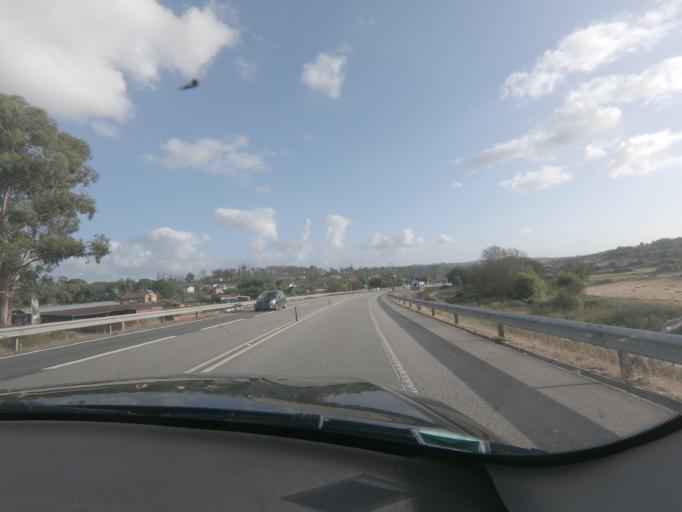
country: PT
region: Viseu
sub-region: Concelho de Tondela
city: Tondela
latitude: 40.5396
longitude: -8.0560
